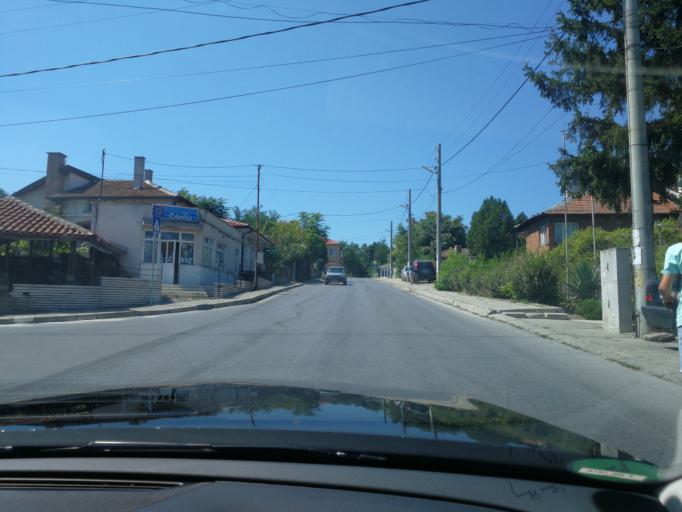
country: BG
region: Khaskovo
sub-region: Obshtina Topolovgrad
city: Topolovgrad
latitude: 42.0851
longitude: 26.3328
